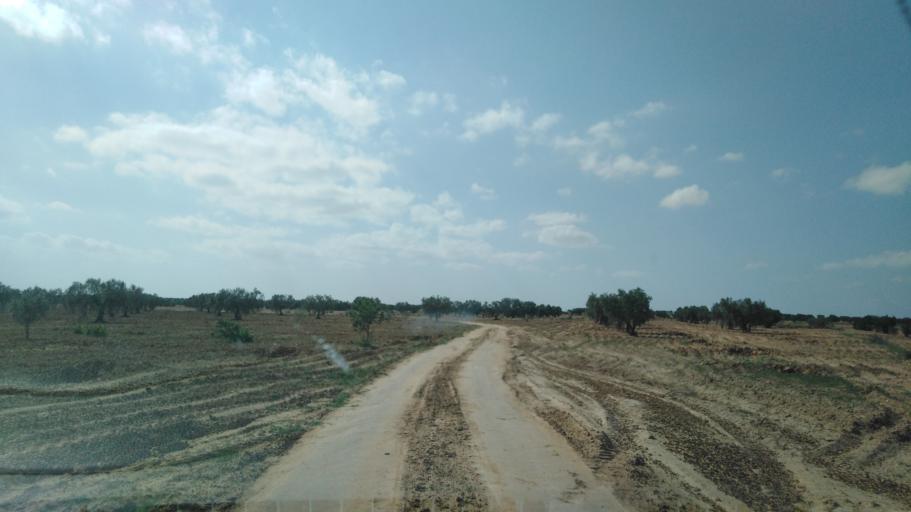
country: TN
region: Safaqis
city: Bi'r `Ali Bin Khalifah
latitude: 34.7984
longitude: 10.3867
